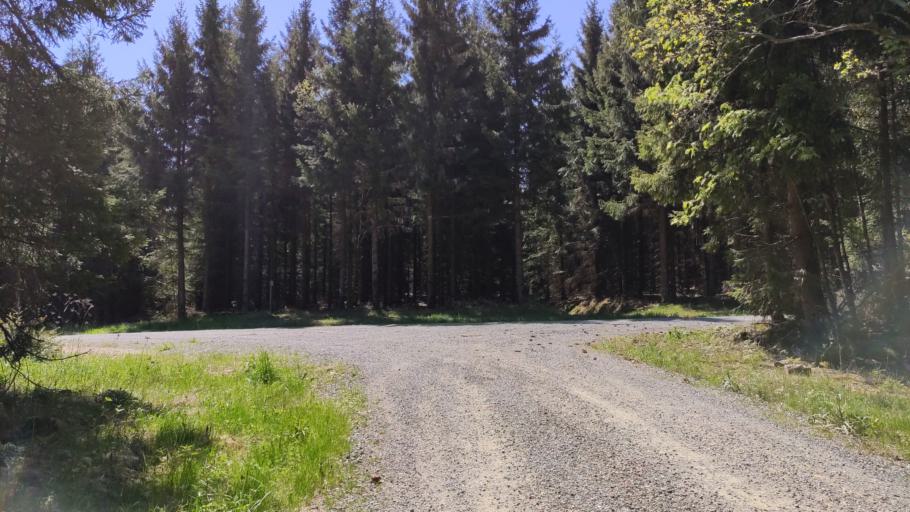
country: DE
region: Bavaria
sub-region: Upper Franconia
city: Tschirn
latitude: 50.4582
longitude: 11.4600
